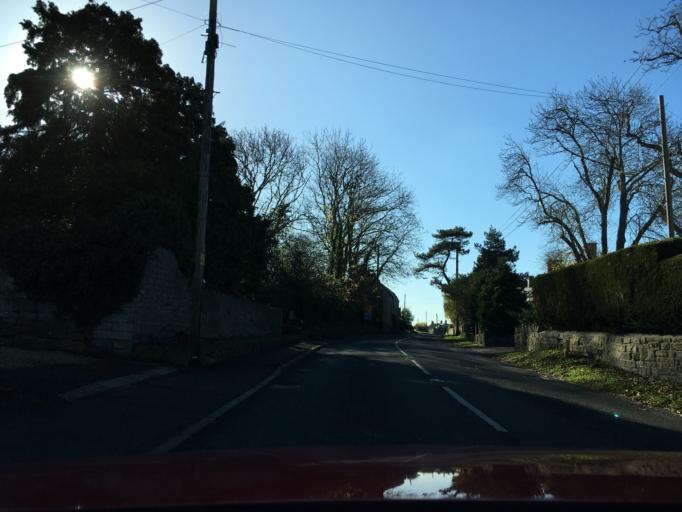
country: GB
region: England
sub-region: Somerset
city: Martock
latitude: 51.0035
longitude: -2.7641
